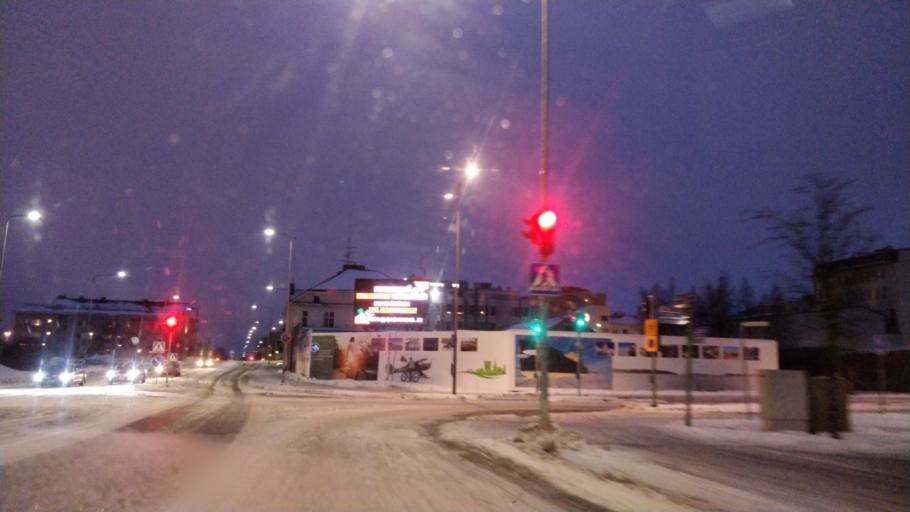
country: FI
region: Lapland
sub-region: Kemi-Tornio
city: Kemi
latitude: 65.7388
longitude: 24.5661
